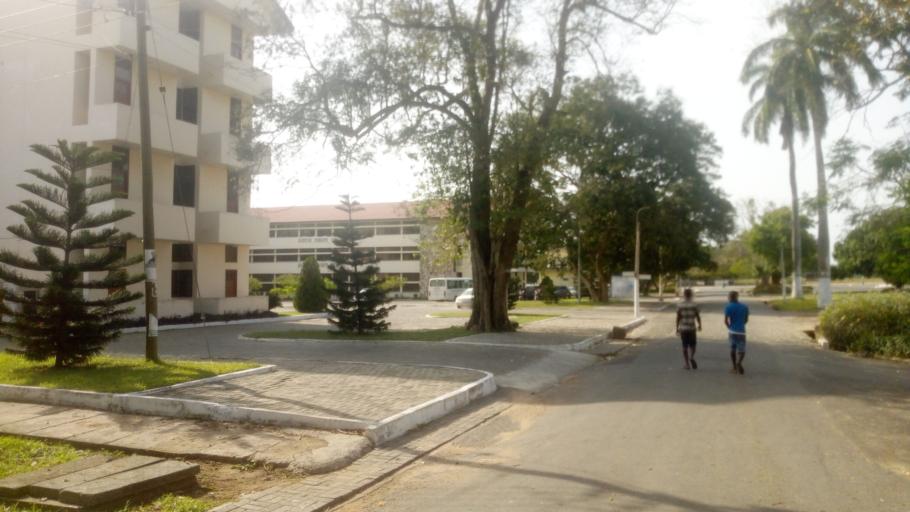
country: GH
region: Central
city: Winneba
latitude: 5.3610
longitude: -0.6330
